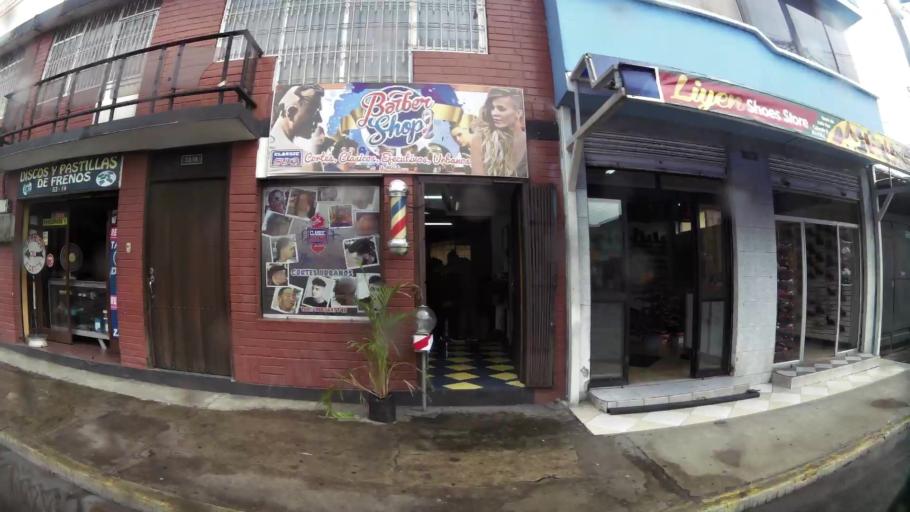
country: EC
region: Pichincha
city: Sangolqui
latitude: -0.2944
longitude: -78.4793
